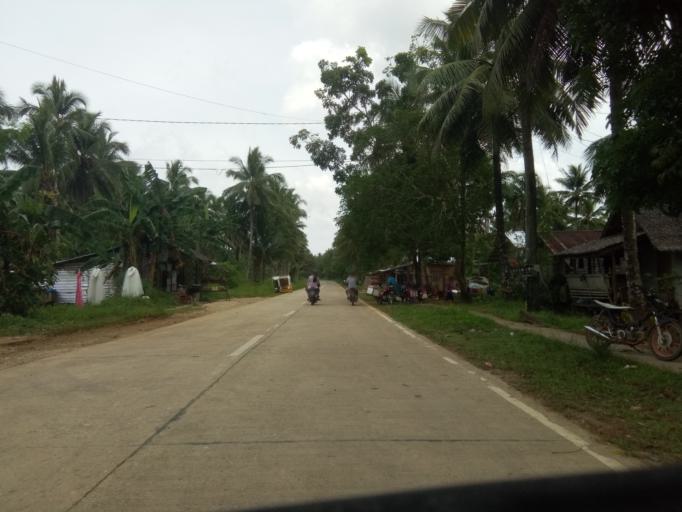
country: PH
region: Caraga
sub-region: Province of Surigao del Norte
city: San Isidro
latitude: 9.9264
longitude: 126.0538
